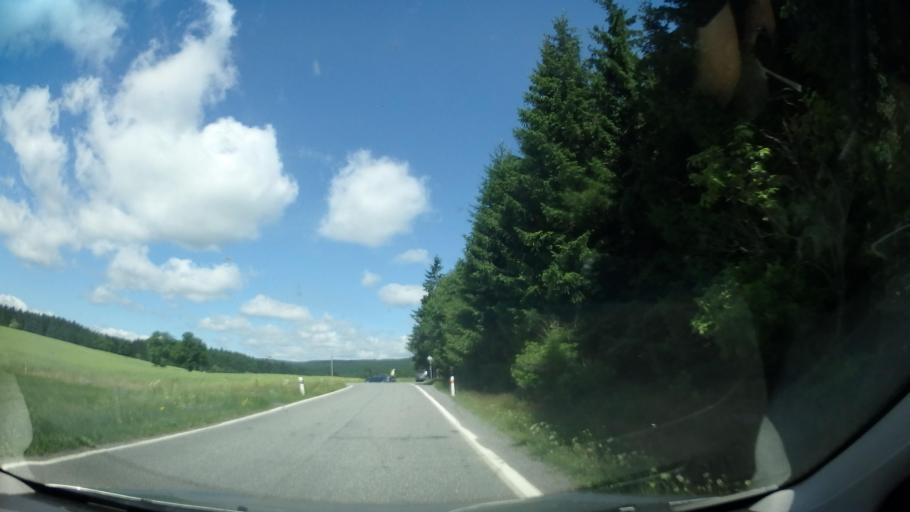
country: CZ
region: Vysocina
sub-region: Okres Zd'ar nad Sazavou
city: Nove Mesto na Morave
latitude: 49.6282
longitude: 16.0696
